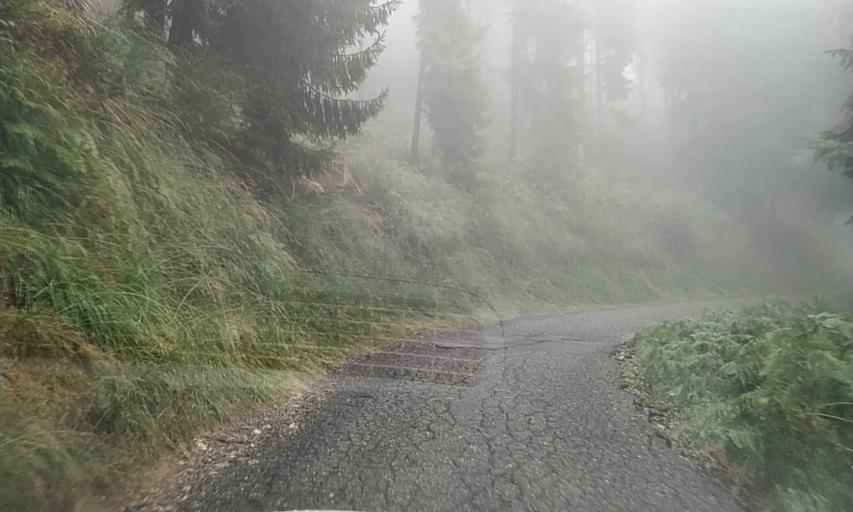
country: IT
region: Piedmont
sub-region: Provincia di Vercelli
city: Civiasco
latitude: 45.8341
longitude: 8.3102
